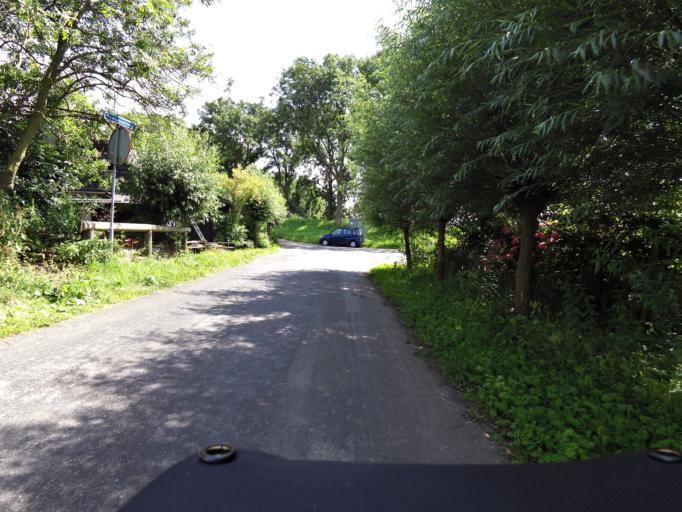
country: NL
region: South Holland
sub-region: Gemeente Albrandswaard
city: Rhoon
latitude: 51.8666
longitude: 4.4032
